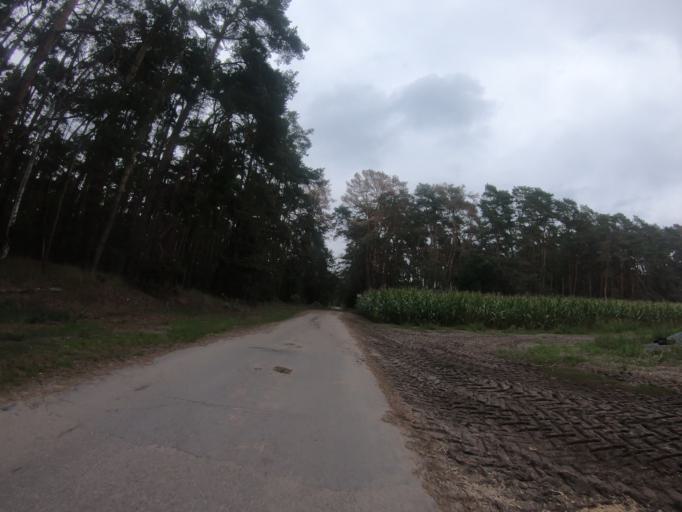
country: DE
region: Lower Saxony
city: Ribbesbuttel
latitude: 52.4448
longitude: 10.5187
